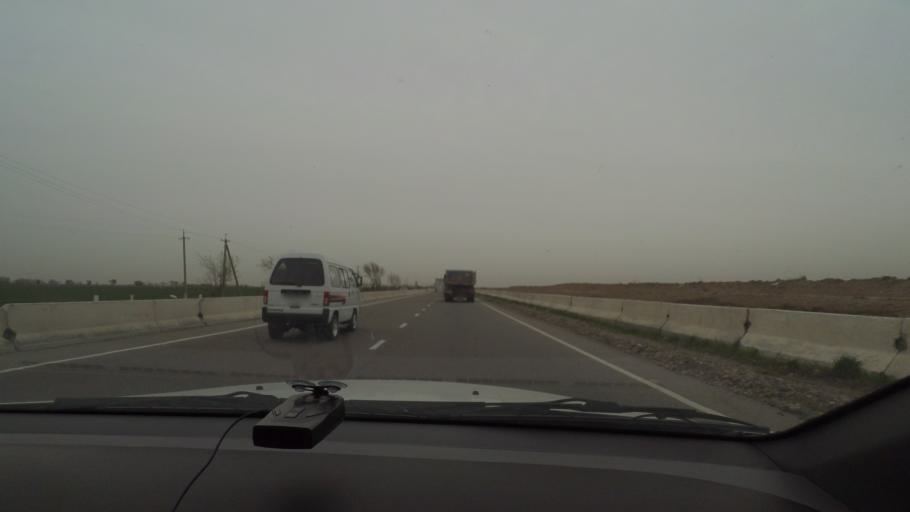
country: UZ
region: Jizzax
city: Gagarin
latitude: 40.4519
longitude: 68.2508
